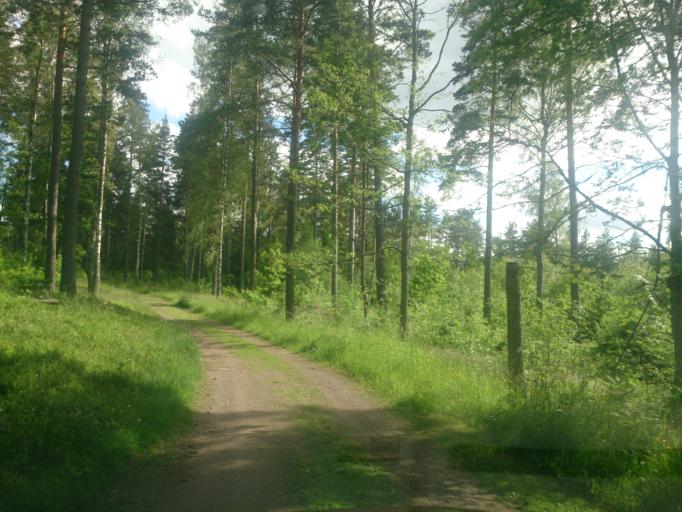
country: SE
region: OEstergoetland
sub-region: Atvidabergs Kommun
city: Atvidaberg
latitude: 58.2097
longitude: 15.9997
